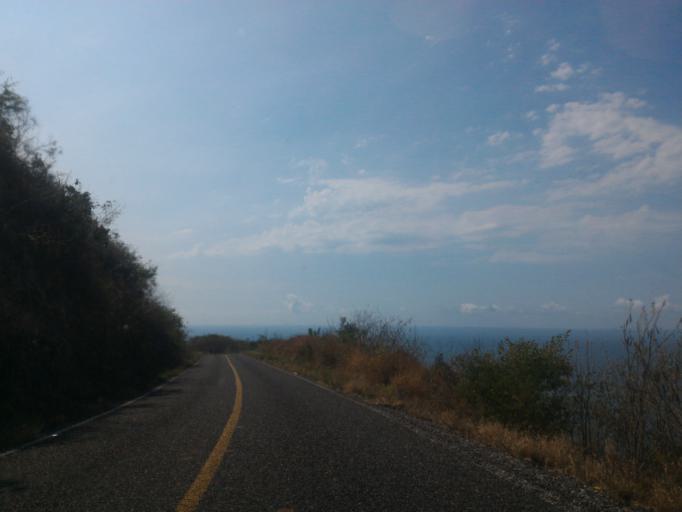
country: MX
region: Michoacan
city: Coahuayana Viejo
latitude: 18.4706
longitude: -103.5582
